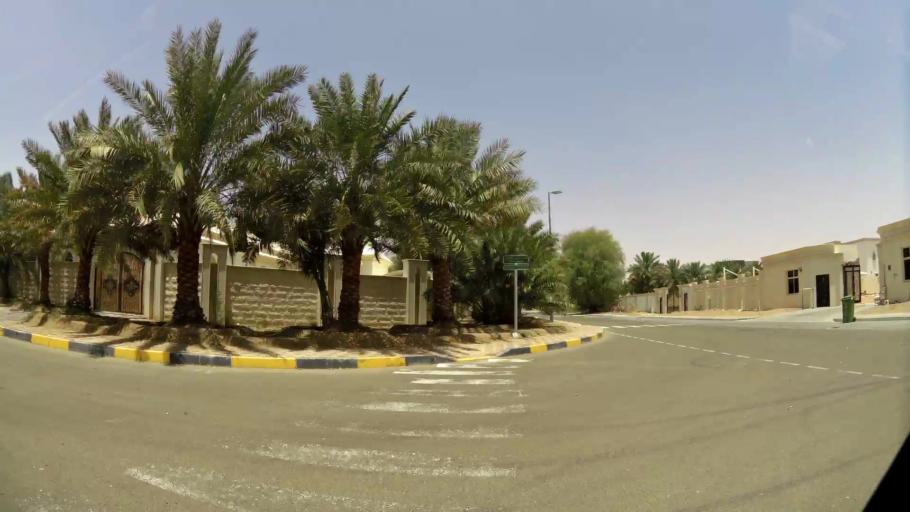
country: OM
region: Al Buraimi
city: Al Buraymi
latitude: 24.2900
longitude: 55.7406
